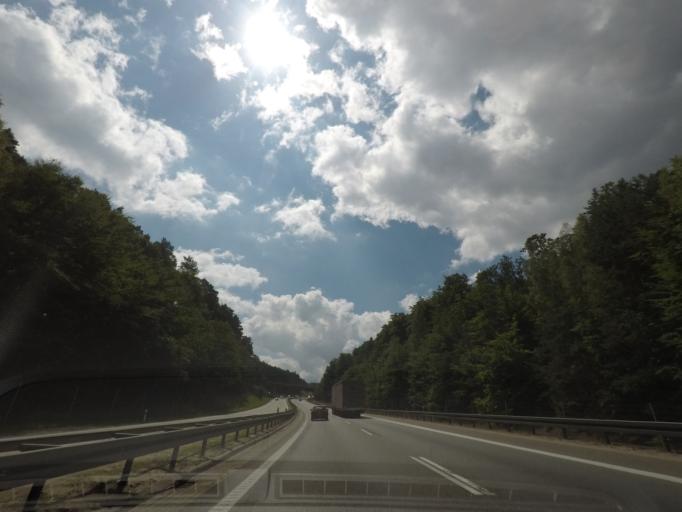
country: PL
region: Pomeranian Voivodeship
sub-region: Gdynia
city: Pogorze
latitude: 54.5207
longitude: 18.4577
